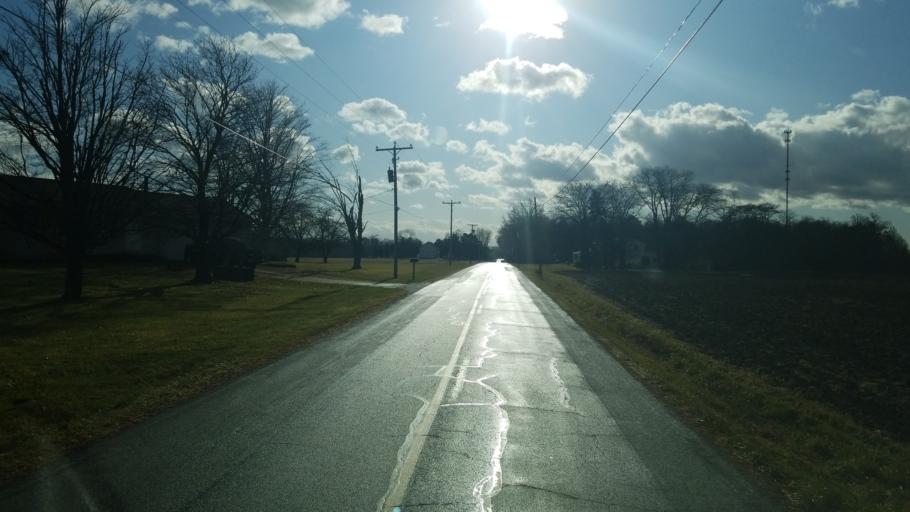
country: US
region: Ohio
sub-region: Marion County
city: Marion
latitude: 40.5324
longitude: -83.0691
